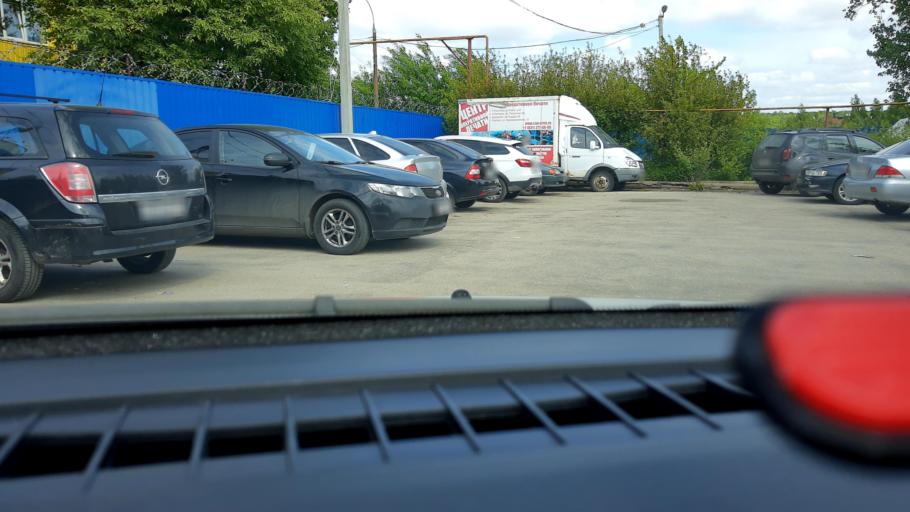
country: RU
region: Nizjnij Novgorod
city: Nizhniy Novgorod
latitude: 56.2427
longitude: 44.0066
